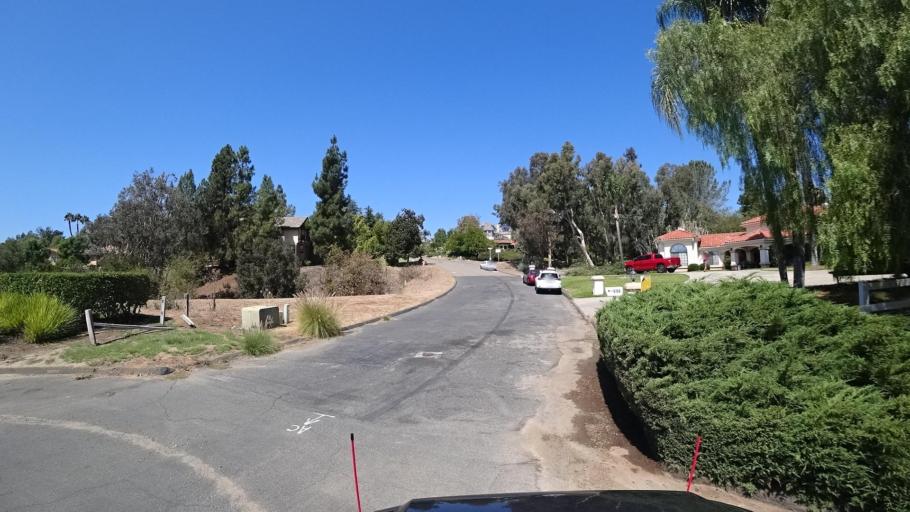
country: US
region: California
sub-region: San Diego County
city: Vista
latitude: 33.1938
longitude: -117.1889
